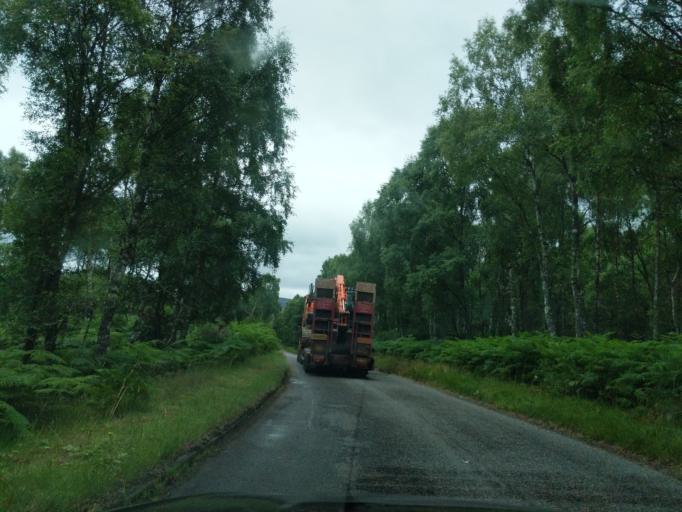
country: GB
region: Scotland
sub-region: Aberdeenshire
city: Ballater
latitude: 57.0707
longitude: -2.9475
